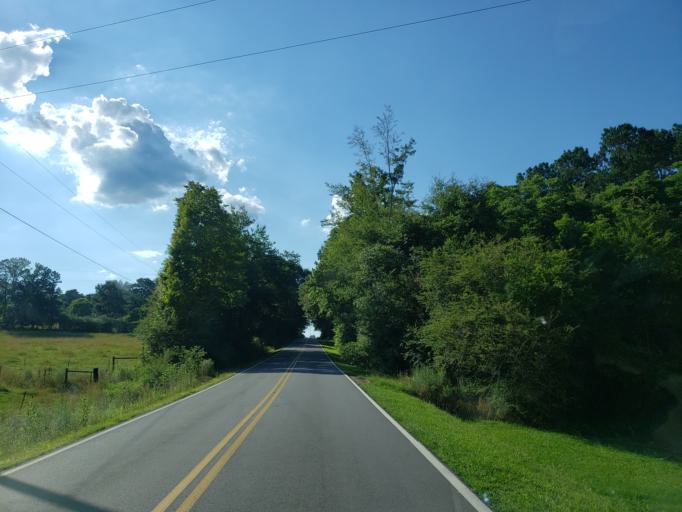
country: US
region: Georgia
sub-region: Haralson County
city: Bremen
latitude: 33.6524
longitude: -85.1115
